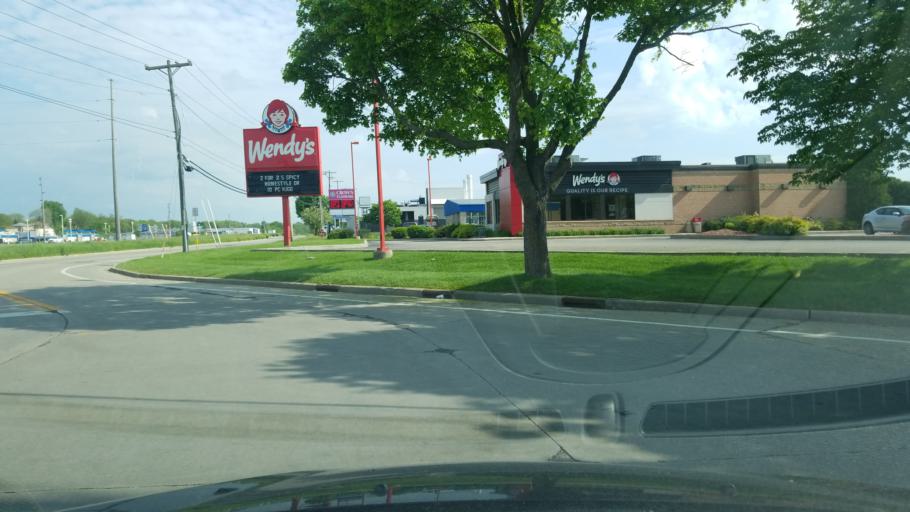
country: US
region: Wisconsin
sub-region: Dane County
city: Monona
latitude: 43.0624
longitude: -89.3085
